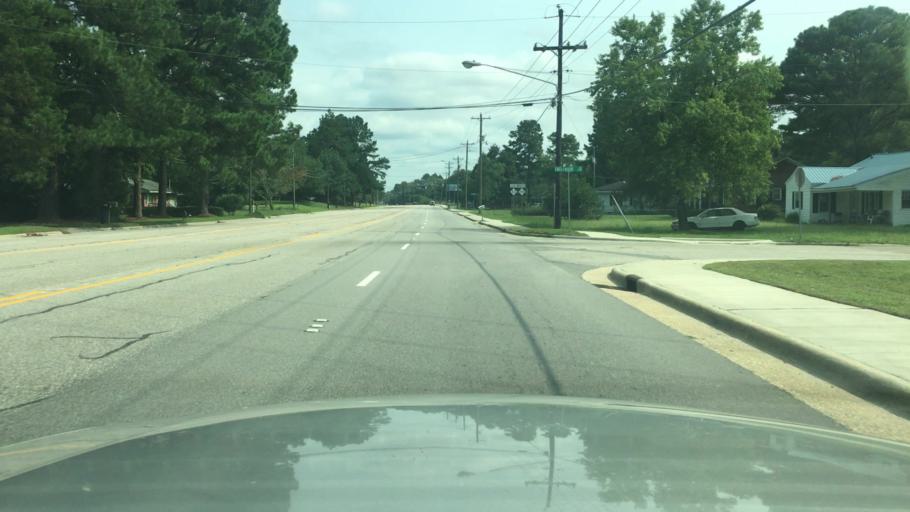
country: US
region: North Carolina
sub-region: Cumberland County
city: Fayetteville
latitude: 35.0271
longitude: -78.8431
